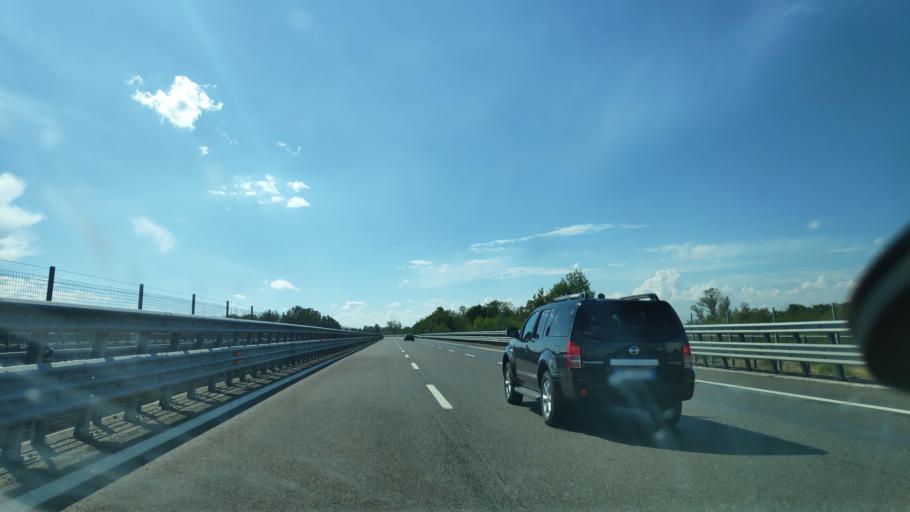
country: IT
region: Piedmont
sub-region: Provincia di Alessandria
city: Castelnuovo Scrivia
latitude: 44.9538
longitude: 8.8713
